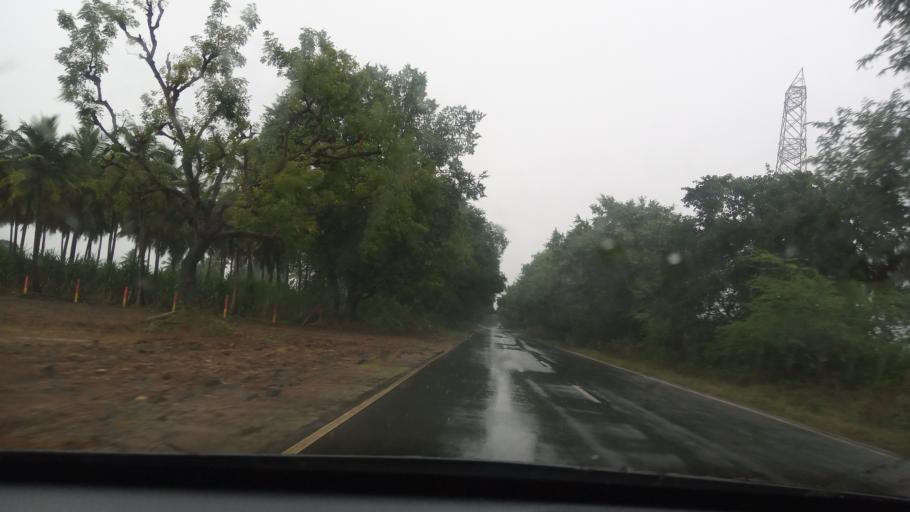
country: IN
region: Tamil Nadu
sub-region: Vellore
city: Kalavai
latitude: 12.8453
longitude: 79.3961
